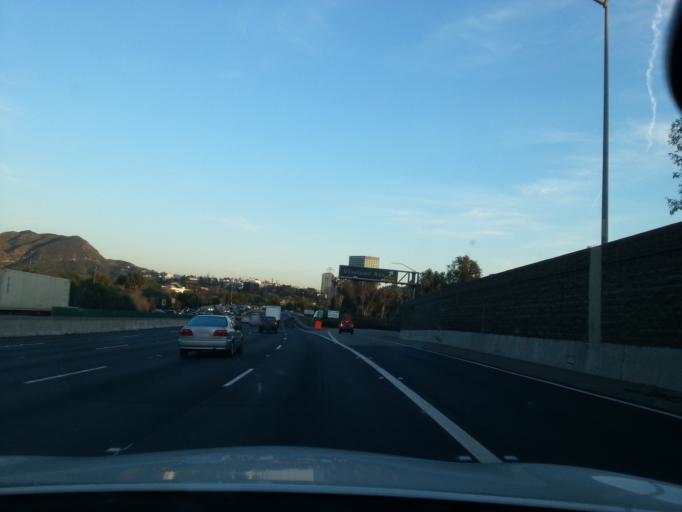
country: US
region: California
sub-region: Los Angeles County
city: Universal City
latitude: 34.1486
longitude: -118.3729
